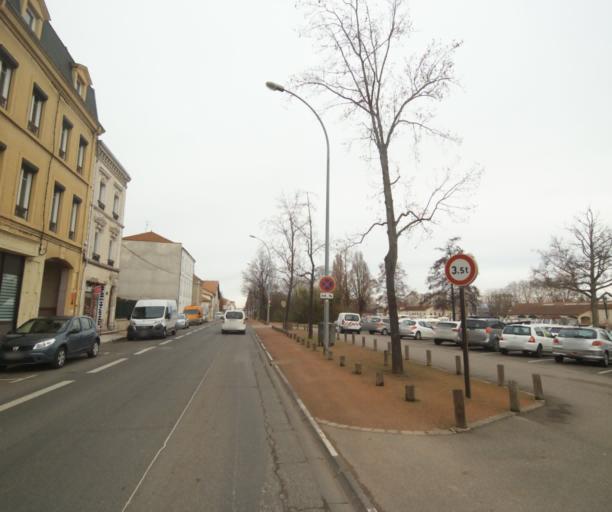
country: FR
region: Rhone-Alpes
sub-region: Departement de la Loire
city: Le Coteau
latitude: 46.0353
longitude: 4.0792
